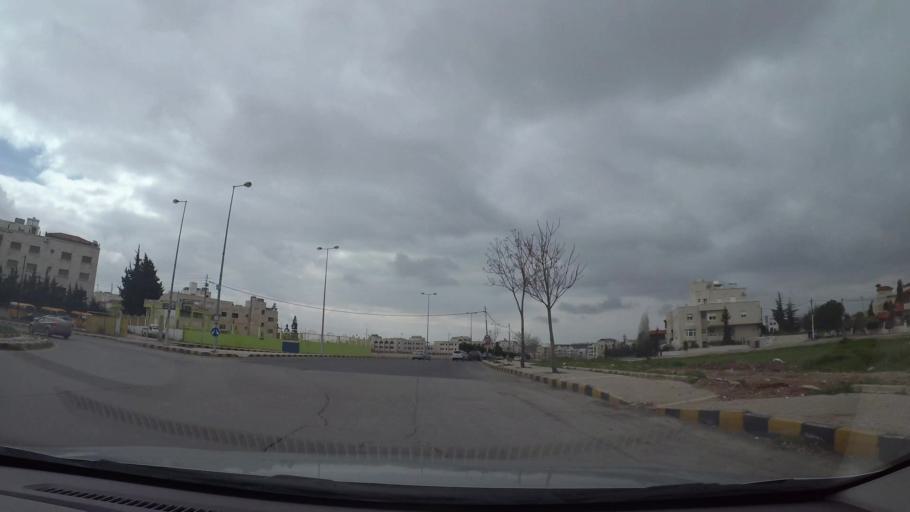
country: JO
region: Amman
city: Al Jubayhah
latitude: 31.9903
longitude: 35.8446
